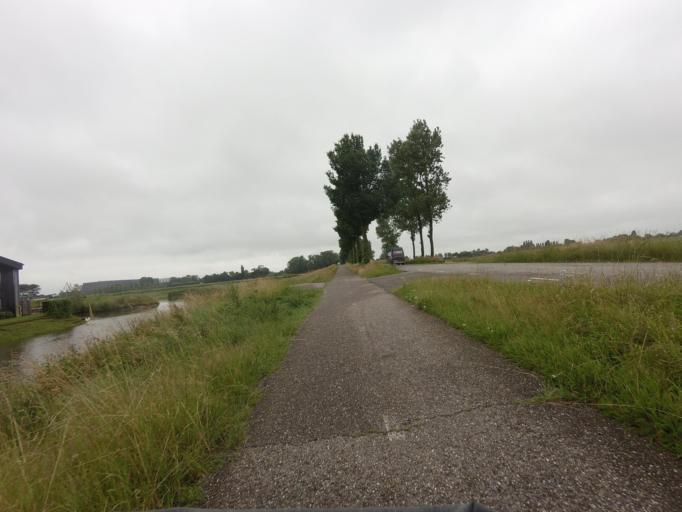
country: NL
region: North Holland
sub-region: Gemeente Opmeer
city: Opmeer
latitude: 52.7631
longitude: 4.8914
